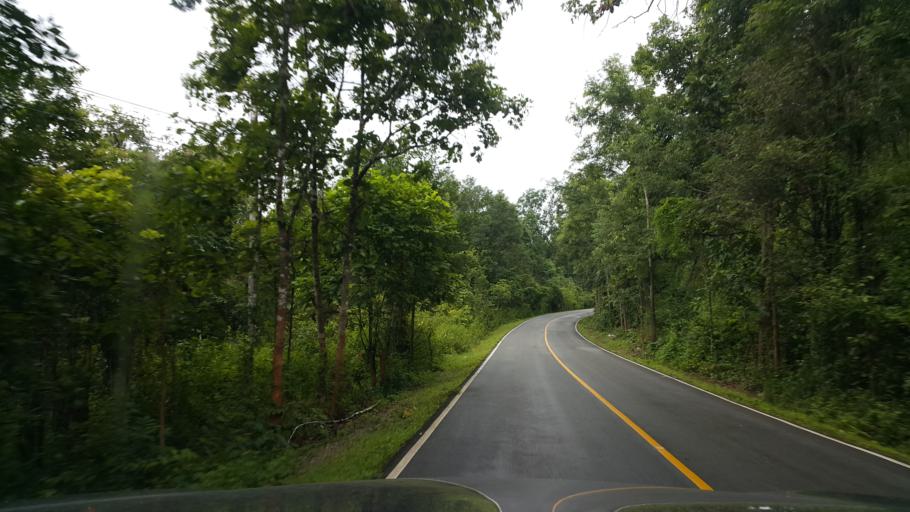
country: TH
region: Chiang Mai
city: Samoeng
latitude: 18.8626
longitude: 98.6671
